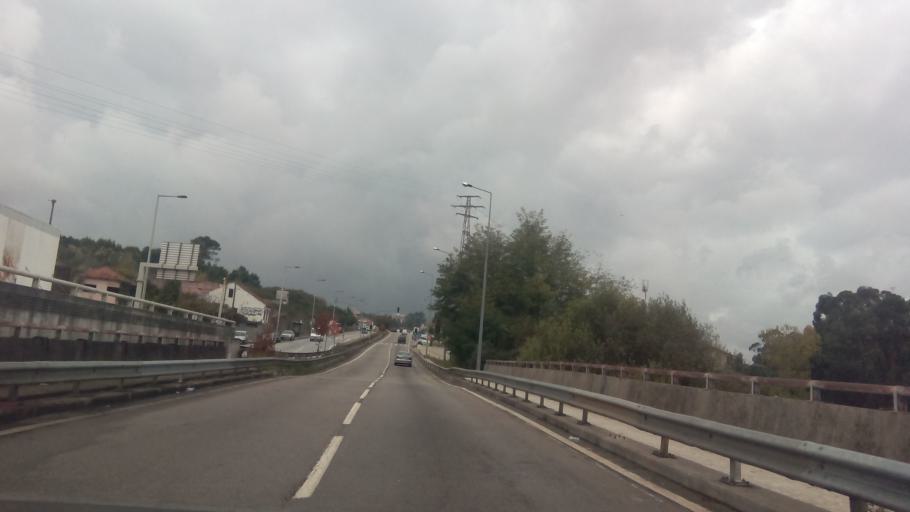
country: PT
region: Porto
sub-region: Gondomar
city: Rio Tinto
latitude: 41.1760
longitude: -8.5661
